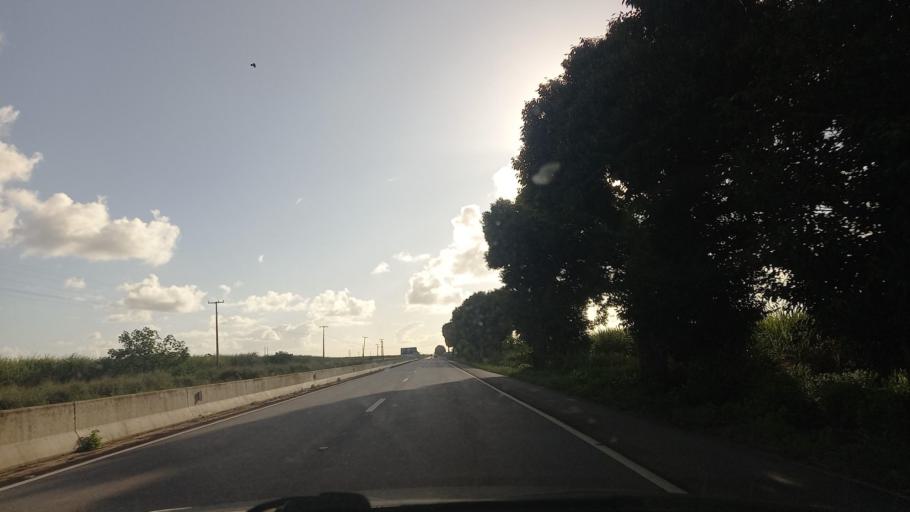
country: BR
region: Alagoas
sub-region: Sao Miguel Dos Campos
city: Sao Miguel dos Campos
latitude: -9.8045
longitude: -36.1321
